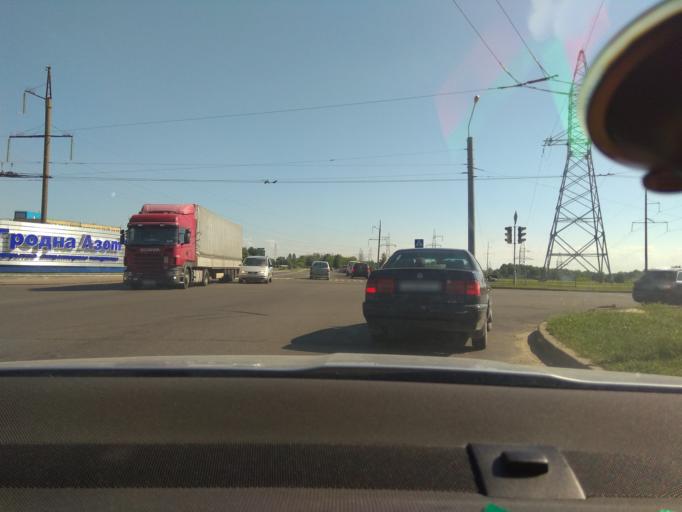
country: BY
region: Grodnenskaya
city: Hrodna
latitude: 53.6724
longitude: 23.8899
